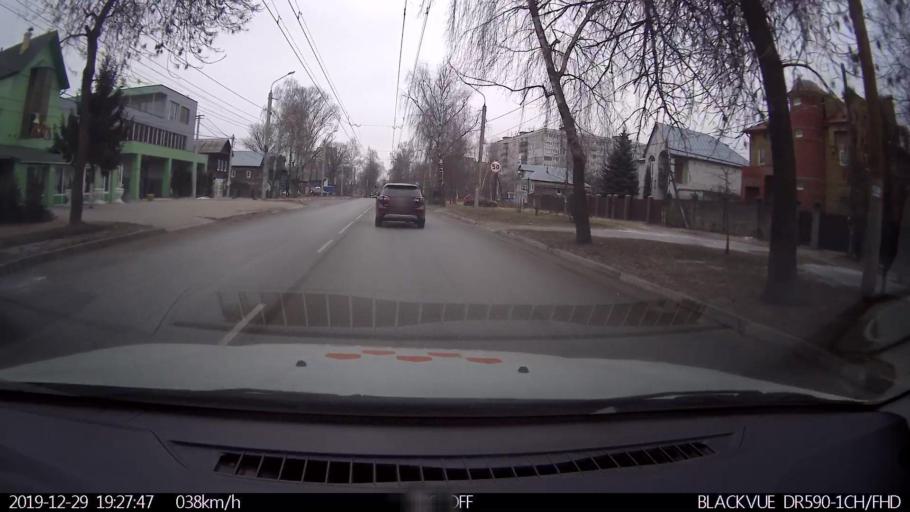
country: RU
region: Nizjnij Novgorod
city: Neklyudovo
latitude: 56.3643
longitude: 43.8518
